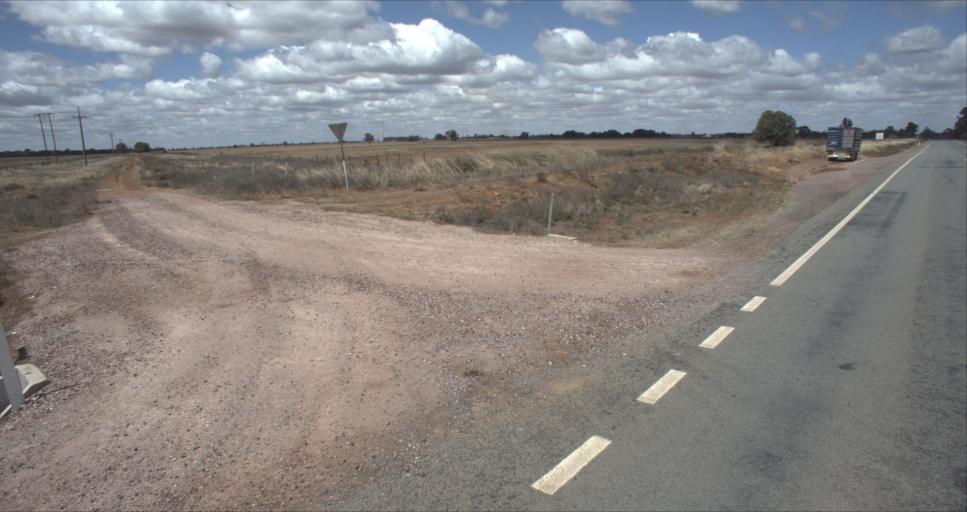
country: AU
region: New South Wales
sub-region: Murrumbidgee Shire
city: Darlington Point
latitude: -34.5105
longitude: 146.1864
